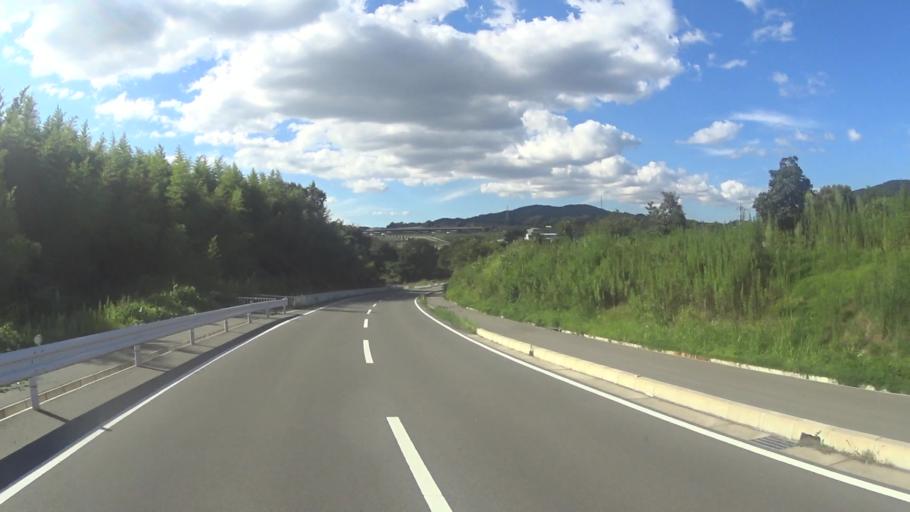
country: JP
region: Kyoto
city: Uji
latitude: 34.8419
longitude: 135.8443
